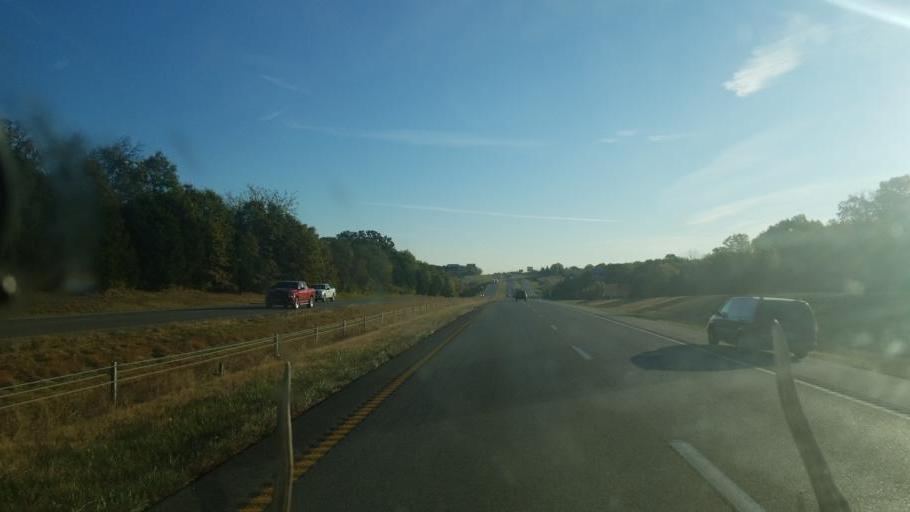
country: US
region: Missouri
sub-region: Warren County
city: Warrenton
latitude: 38.8205
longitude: -91.0943
